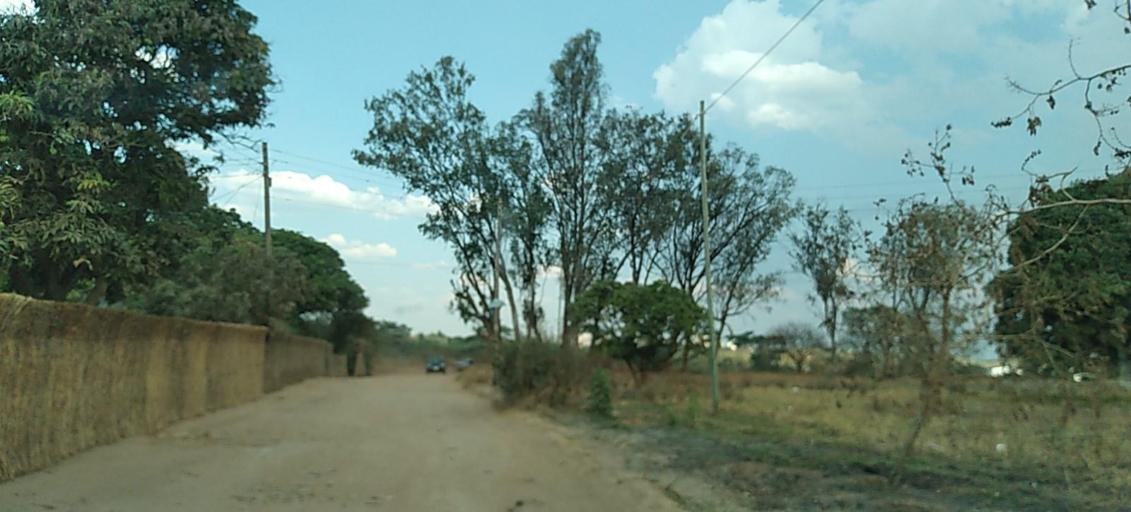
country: ZM
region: Lusaka
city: Lusaka
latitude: -15.5420
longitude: 28.2440
